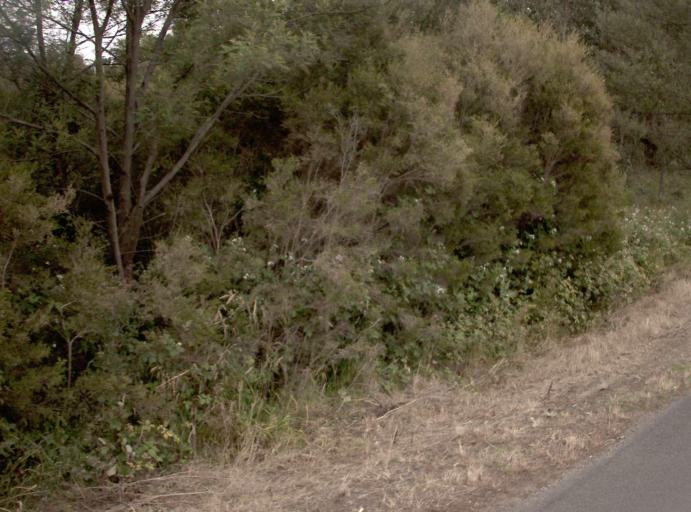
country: AU
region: Victoria
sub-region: Wellington
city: Sale
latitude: -38.2447
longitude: 147.0556
